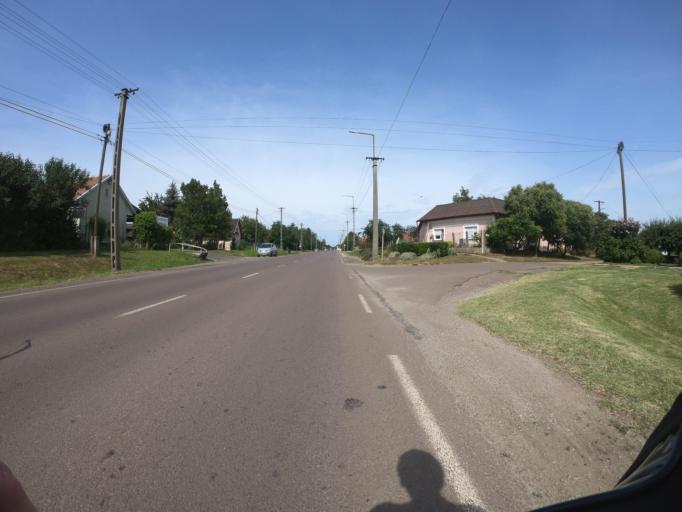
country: HU
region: Jasz-Nagykun-Szolnok
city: Tiszafured
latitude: 47.6060
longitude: 20.7729
